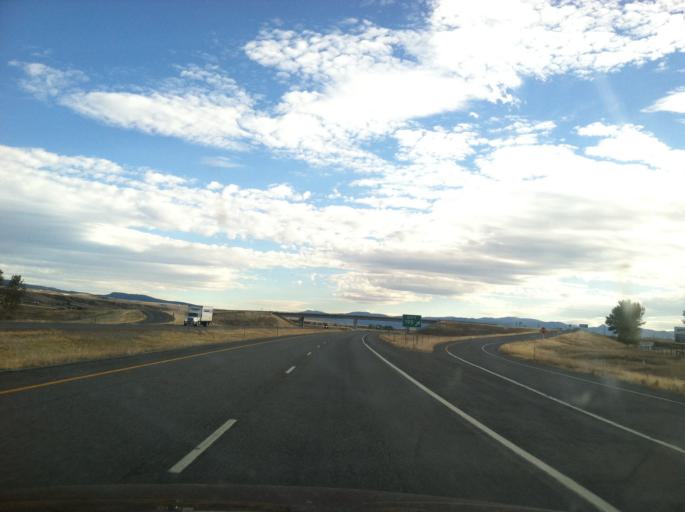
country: US
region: Montana
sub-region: Deer Lodge County
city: Warm Springs
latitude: 46.2731
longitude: -112.7476
